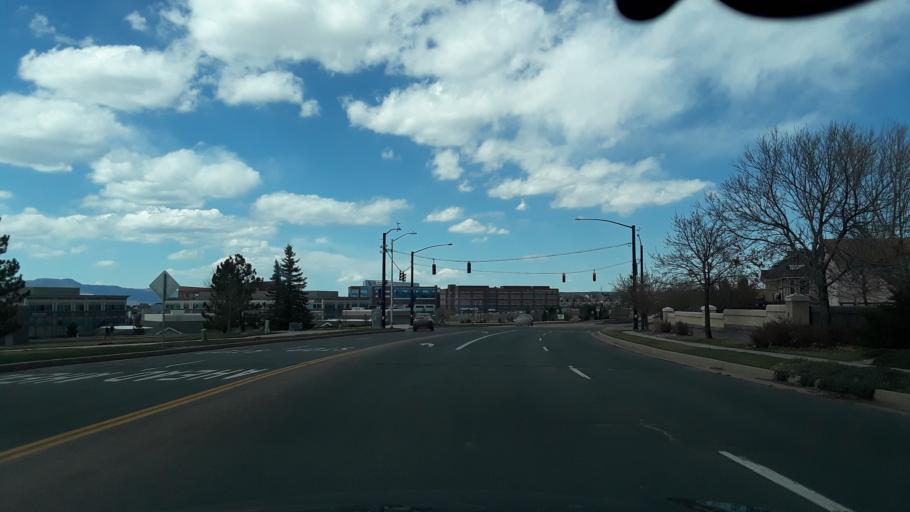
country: US
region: Colorado
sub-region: El Paso County
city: Black Forest
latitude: 38.9629
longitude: -104.7507
